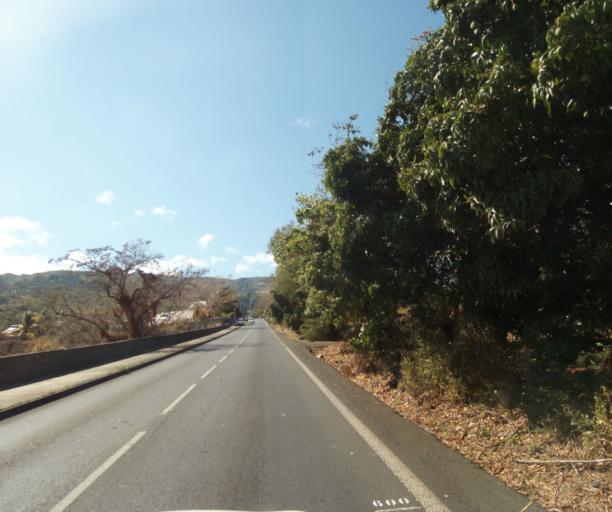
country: RE
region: Reunion
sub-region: Reunion
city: La Possession
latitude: -20.9795
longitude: 55.3321
